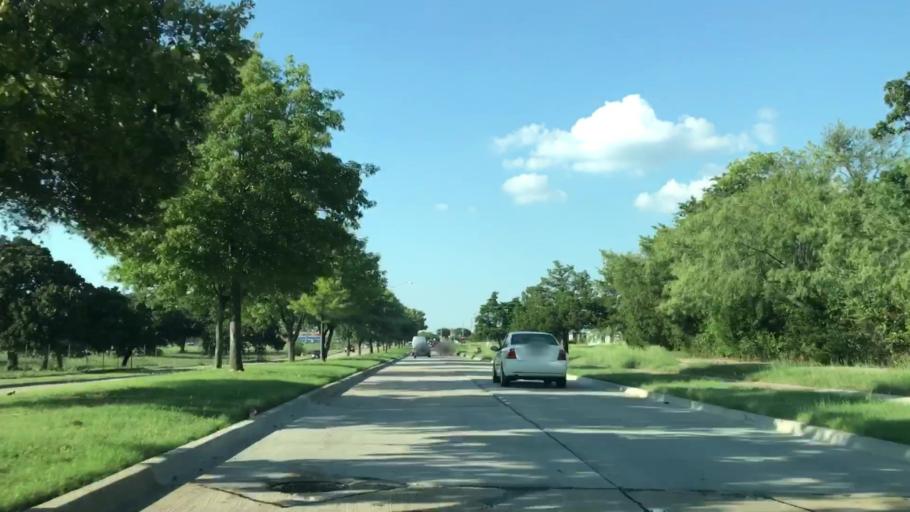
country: US
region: Texas
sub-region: Denton County
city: Lewisville
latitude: 33.0013
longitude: -97.0065
